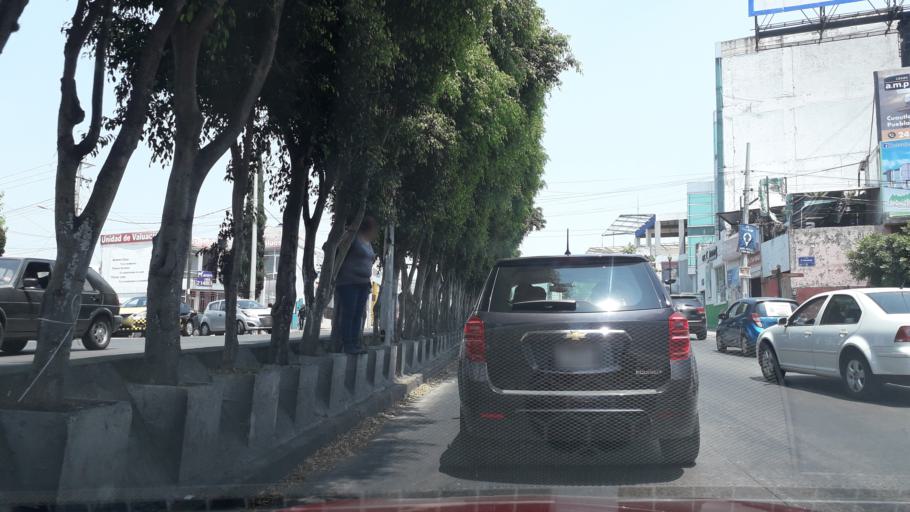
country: MX
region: Puebla
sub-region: San Pedro Cholula
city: Santiago Momoxpan
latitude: 19.0510
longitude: -98.2382
